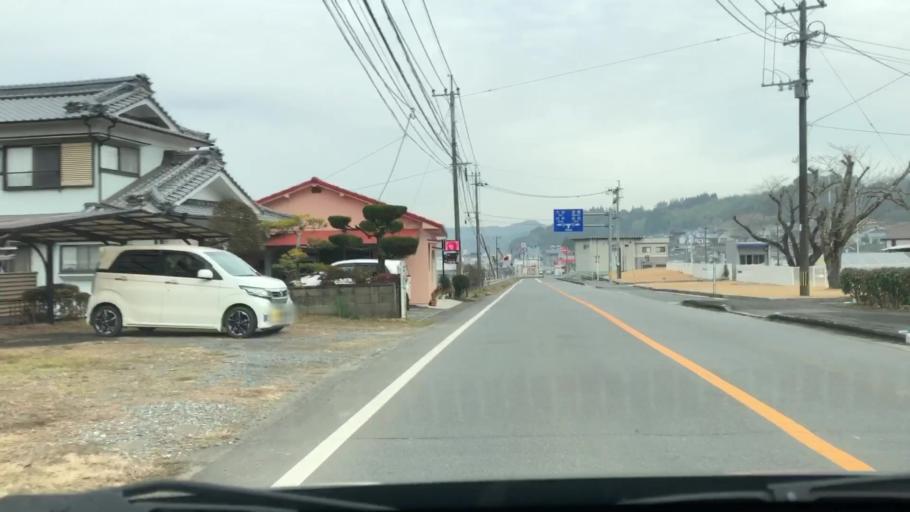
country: JP
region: Oita
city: Usuki
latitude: 33.0308
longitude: 131.6882
